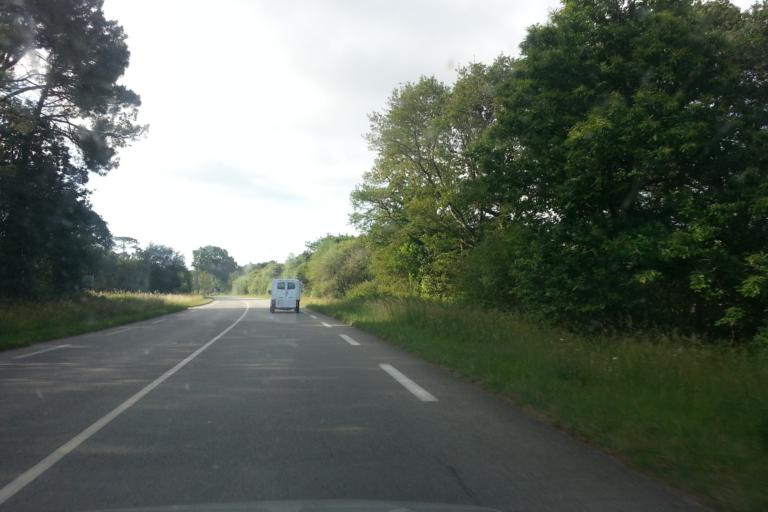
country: FR
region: Brittany
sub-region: Departement du Morbihan
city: Merlevenez
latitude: 47.7204
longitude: -3.2300
